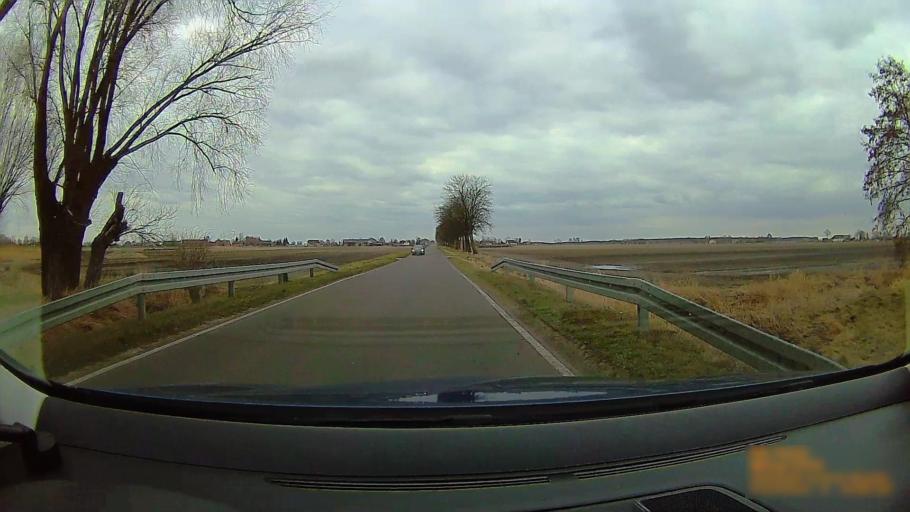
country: PL
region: Greater Poland Voivodeship
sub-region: Powiat koninski
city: Rychwal
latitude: 52.1000
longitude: 18.1019
